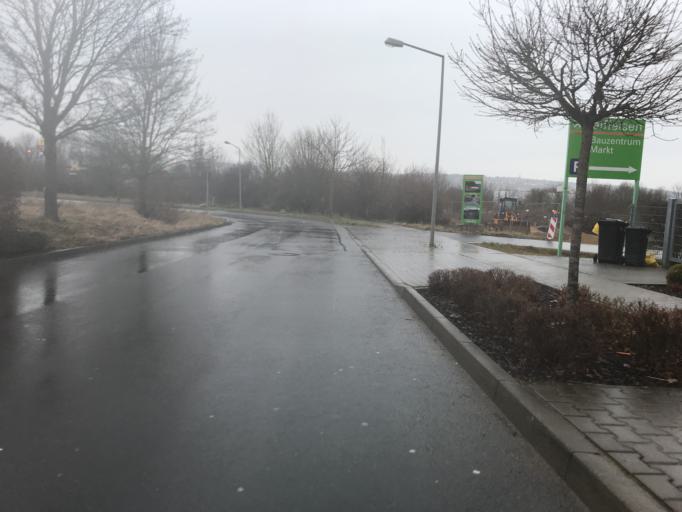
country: DE
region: Rheinland-Pfalz
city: Nieder-Olm
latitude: 49.9126
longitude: 8.1814
